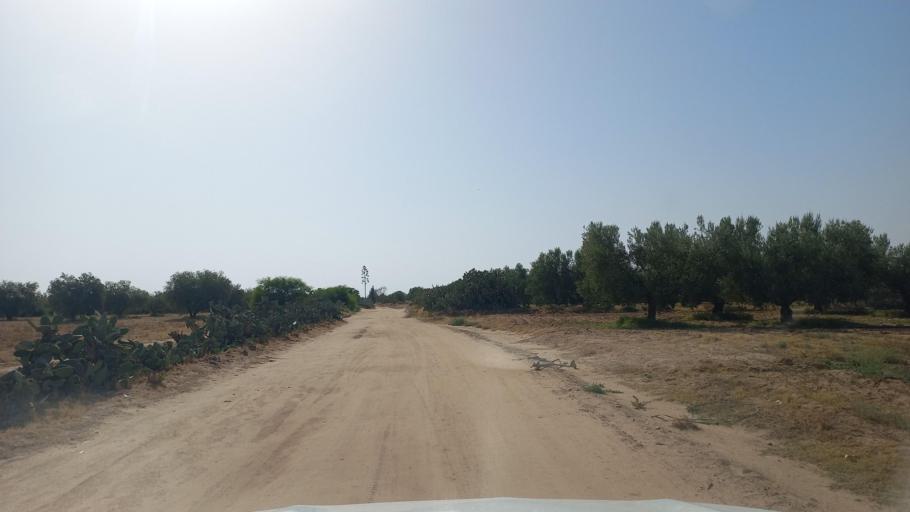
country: TN
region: Al Qasrayn
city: Kasserine
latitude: 35.2500
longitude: 9.0317
